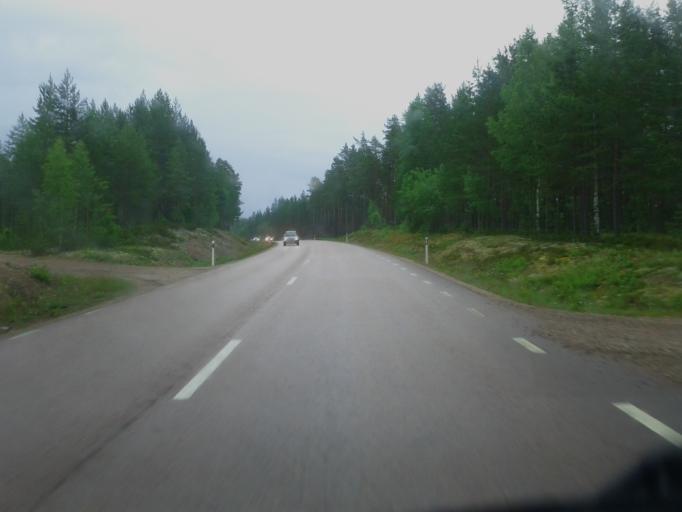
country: SE
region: Dalarna
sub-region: Leksand Municipality
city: Siljansnas
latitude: 60.9375
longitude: 14.7554
